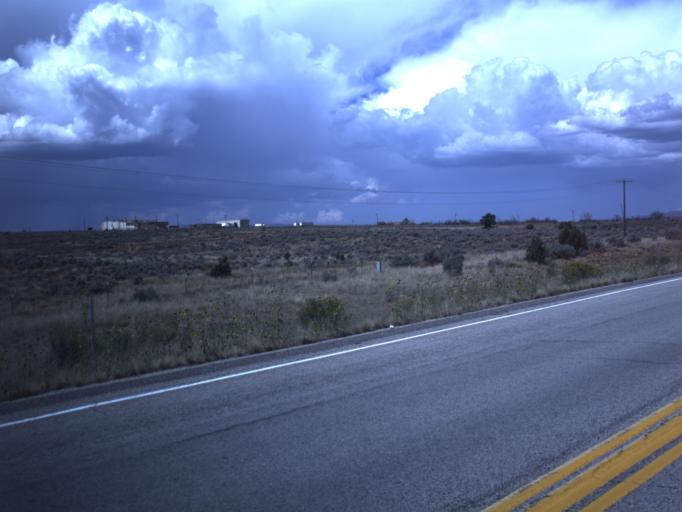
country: US
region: Utah
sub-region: San Juan County
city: Blanding
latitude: 37.5302
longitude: -109.4941
